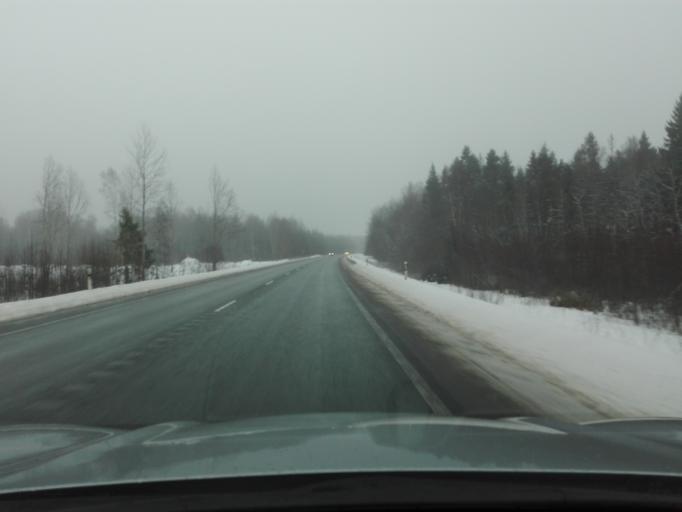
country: EE
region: Raplamaa
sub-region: Kohila vald
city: Kohila
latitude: 59.1359
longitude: 24.7920
